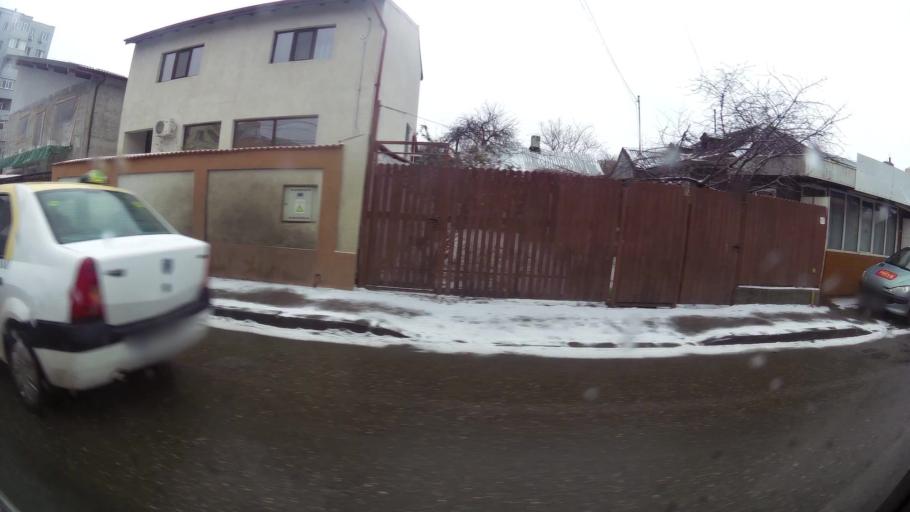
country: RO
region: Prahova
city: Ploiesti
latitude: 44.9497
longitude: 26.0100
